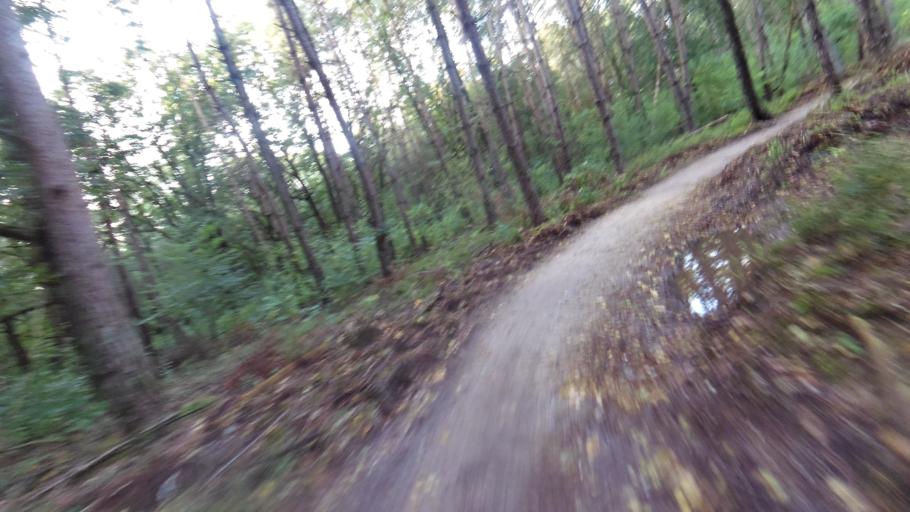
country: NL
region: Utrecht
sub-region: Gemeente Utrechtse Heuvelrug
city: Overberg
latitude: 52.0059
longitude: 5.5055
